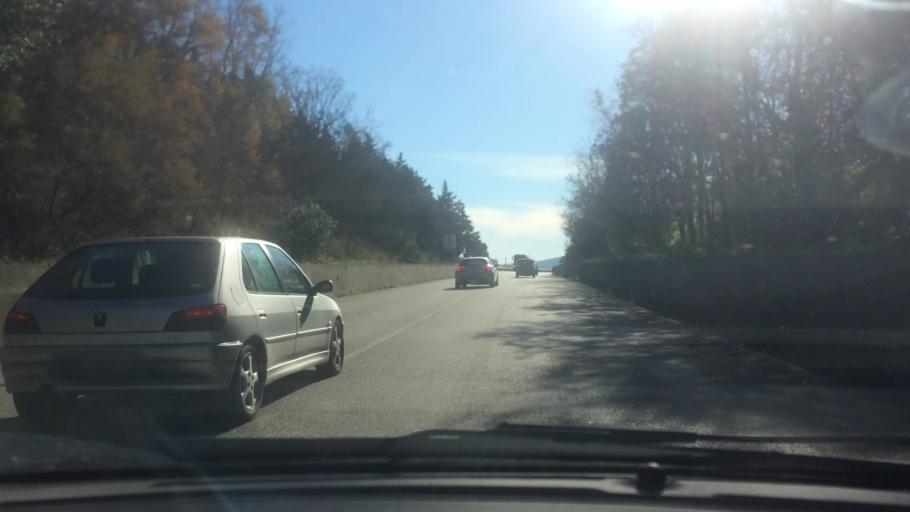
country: IT
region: Basilicate
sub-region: Provincia di Matera
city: Pomarico
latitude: 40.5892
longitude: 16.5749
